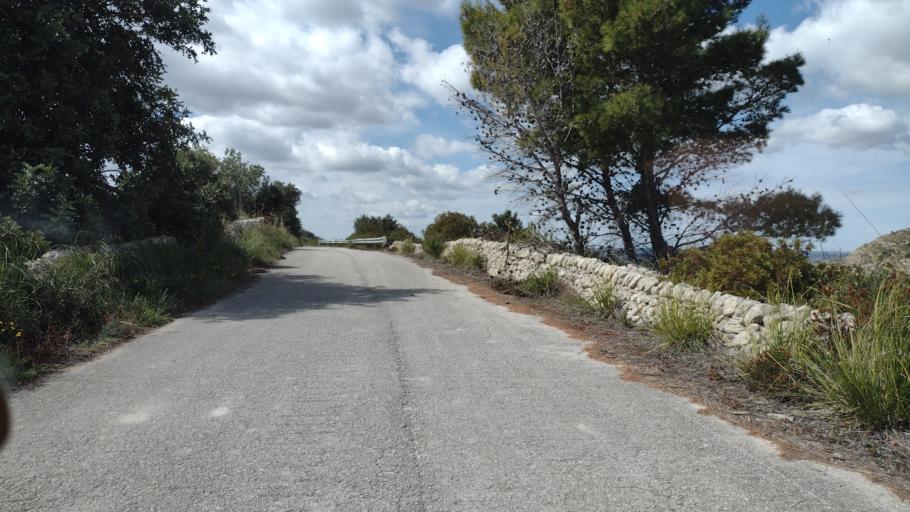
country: IT
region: Sicily
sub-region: Provincia di Siracusa
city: Rosolini
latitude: 36.8994
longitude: 14.9801
